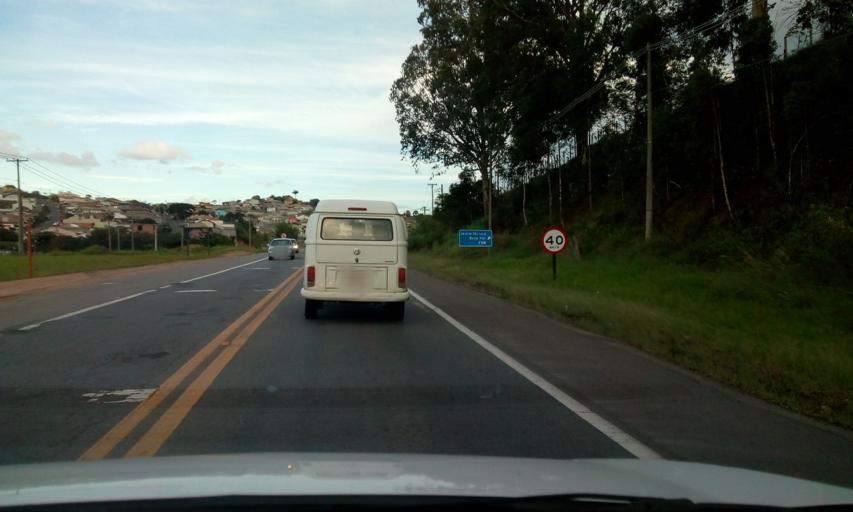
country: BR
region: Sao Paulo
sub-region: Itatiba
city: Itatiba
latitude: -23.0145
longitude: -46.8288
